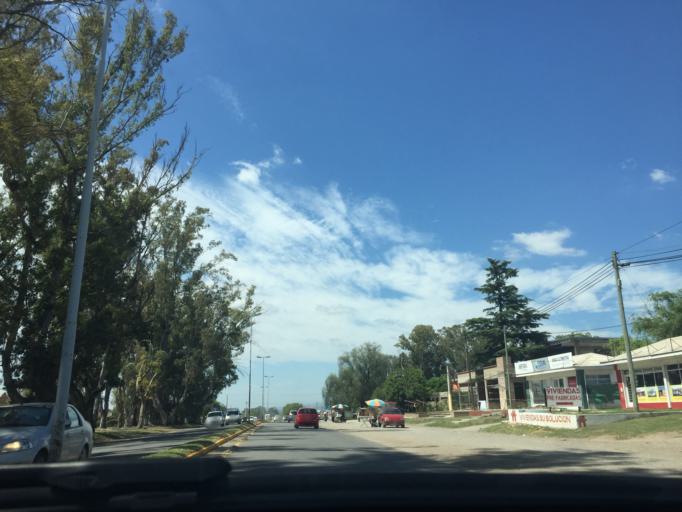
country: AR
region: Cordoba
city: Alta Gracia
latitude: -31.6606
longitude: -64.4098
